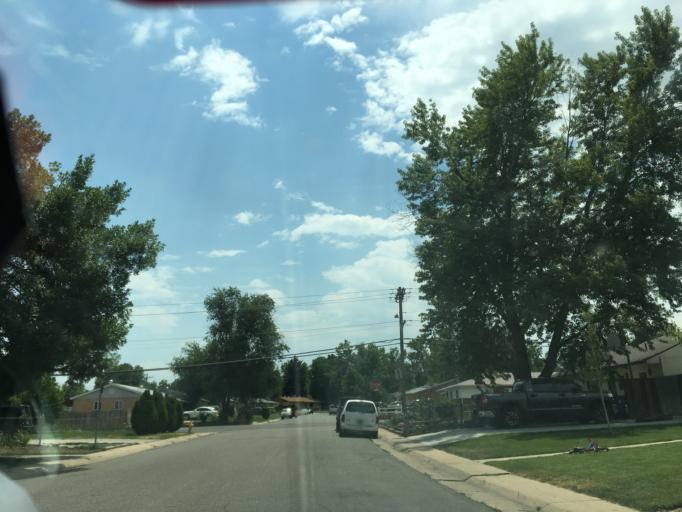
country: US
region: Colorado
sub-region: Arapahoe County
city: Sheridan
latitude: 39.6829
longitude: -105.0354
